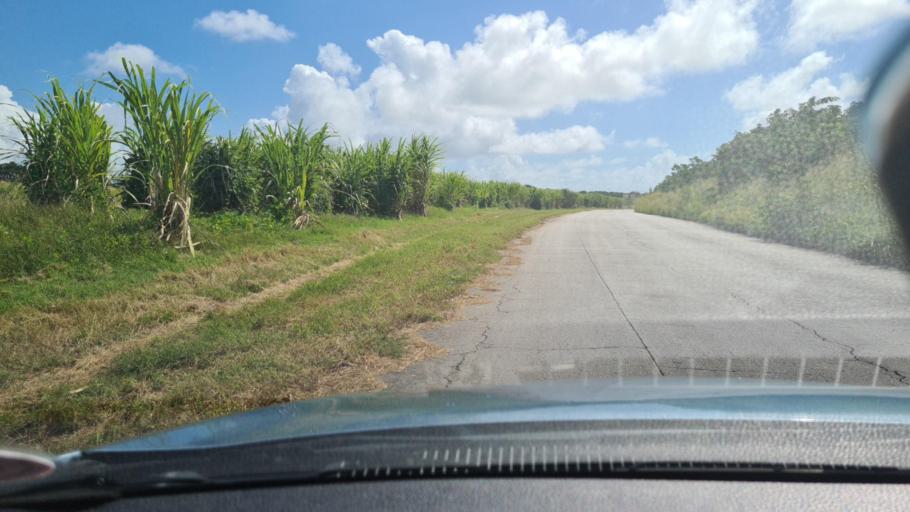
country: BB
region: Christ Church
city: Oistins
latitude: 13.0856
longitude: -59.5378
